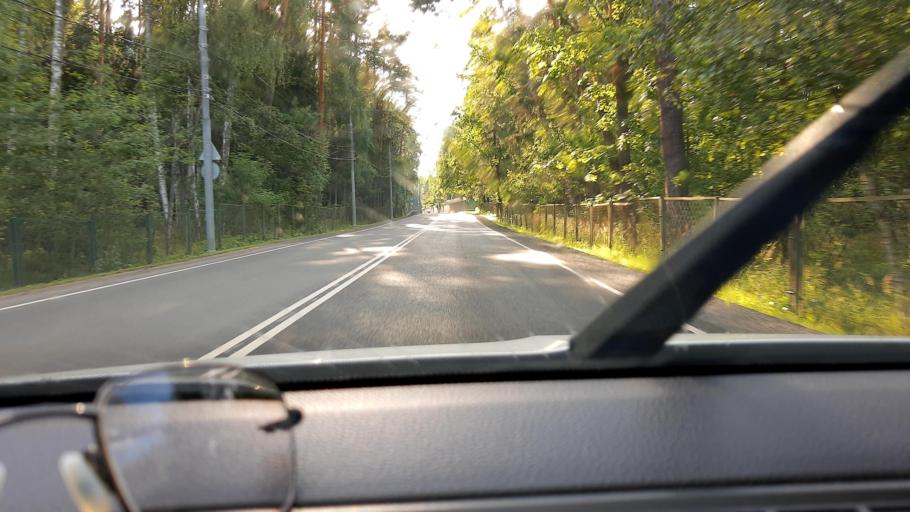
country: RU
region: Moskovskaya
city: Nikolina Gora
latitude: 55.7160
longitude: 36.9697
